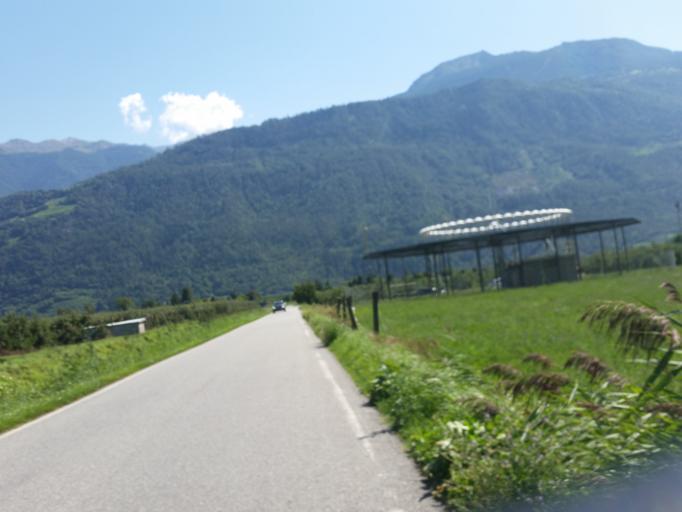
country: CH
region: Valais
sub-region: Conthey District
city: Vetroz
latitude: 46.2160
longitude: 7.2887
